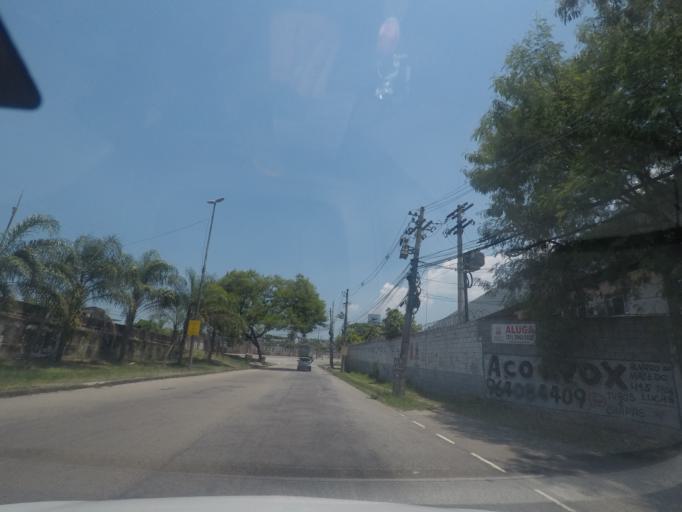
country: BR
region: Rio de Janeiro
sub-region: Duque De Caxias
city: Duque de Caxias
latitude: -22.8029
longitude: -43.3059
